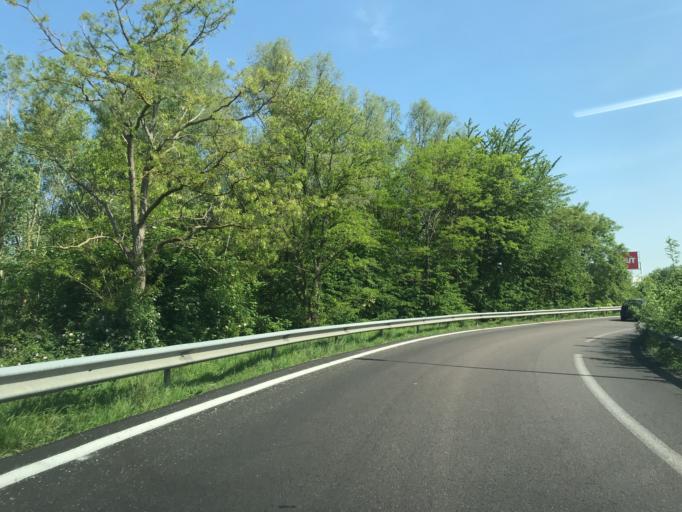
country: FR
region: Haute-Normandie
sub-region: Departement de la Seine-Maritime
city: Oissel
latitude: 49.3263
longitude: 1.0904
